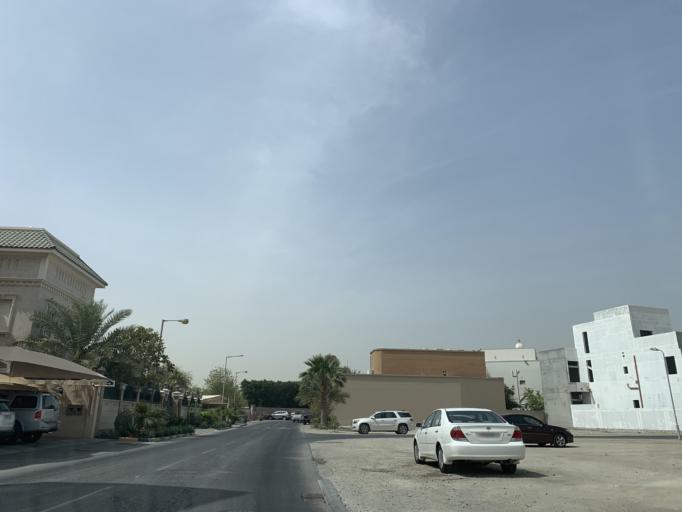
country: BH
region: Northern
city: Madinat `Isa
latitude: 26.1729
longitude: 50.5701
